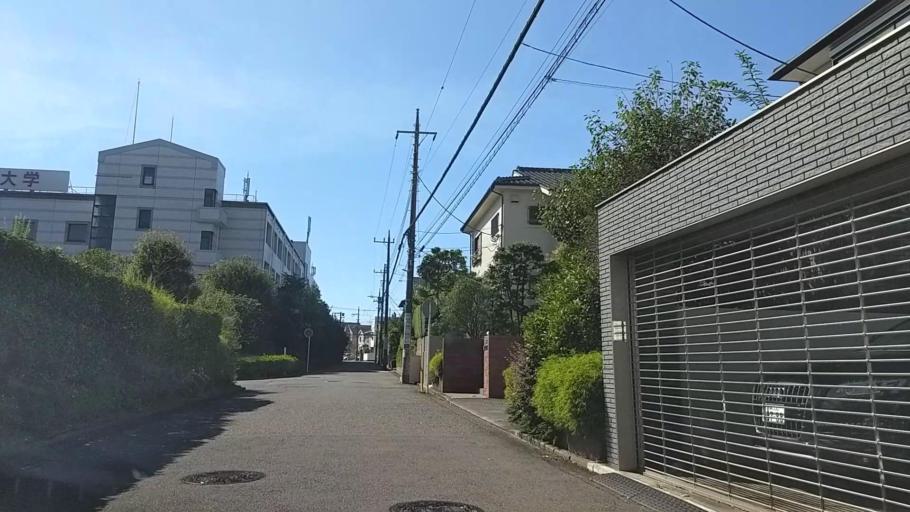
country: JP
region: Tokyo
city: Chofugaoka
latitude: 35.5753
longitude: 139.5602
